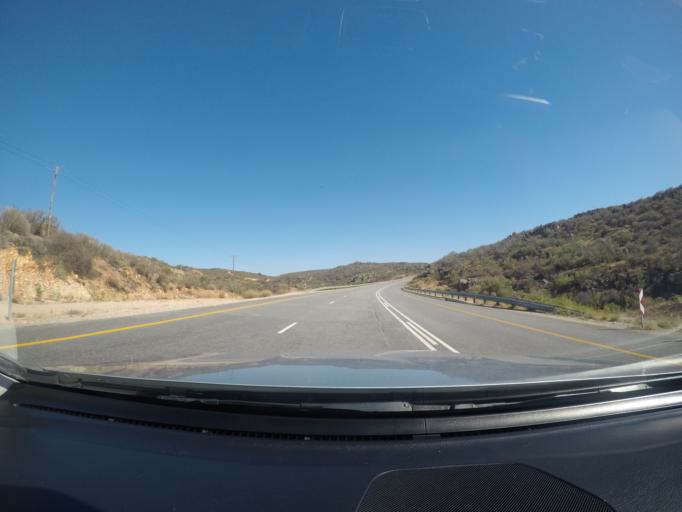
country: ZA
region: Western Cape
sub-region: West Coast District Municipality
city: Clanwilliam
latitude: -32.3402
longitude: 18.9244
